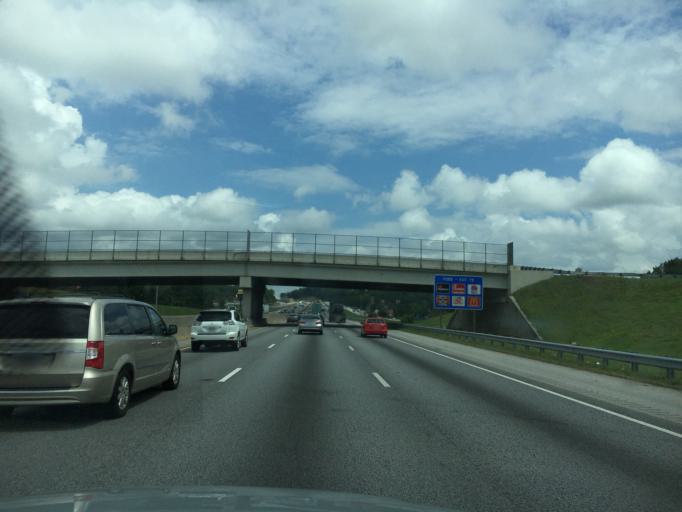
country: US
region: Georgia
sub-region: DeKalb County
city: Lithonia
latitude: 33.7024
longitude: -84.1245
